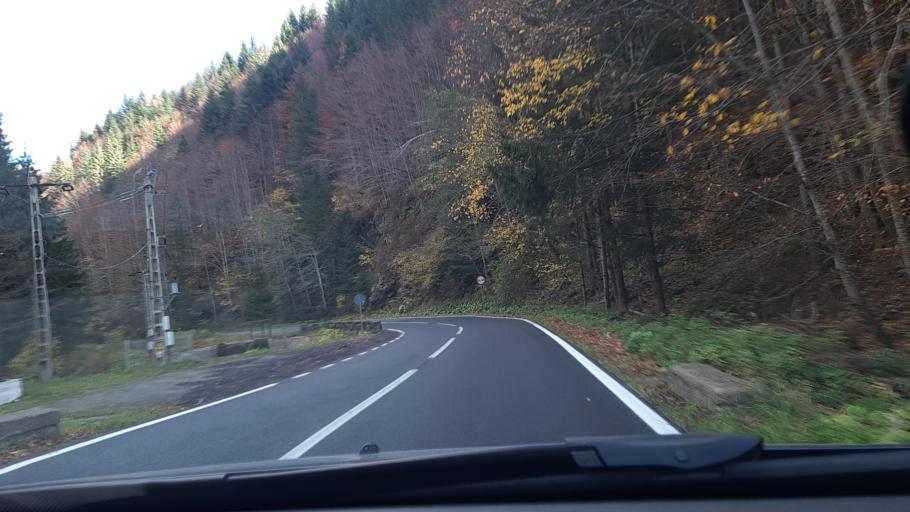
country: RO
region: Valcea
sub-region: Comuna Voineasa
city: Voineasa
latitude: 45.4356
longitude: 23.8684
